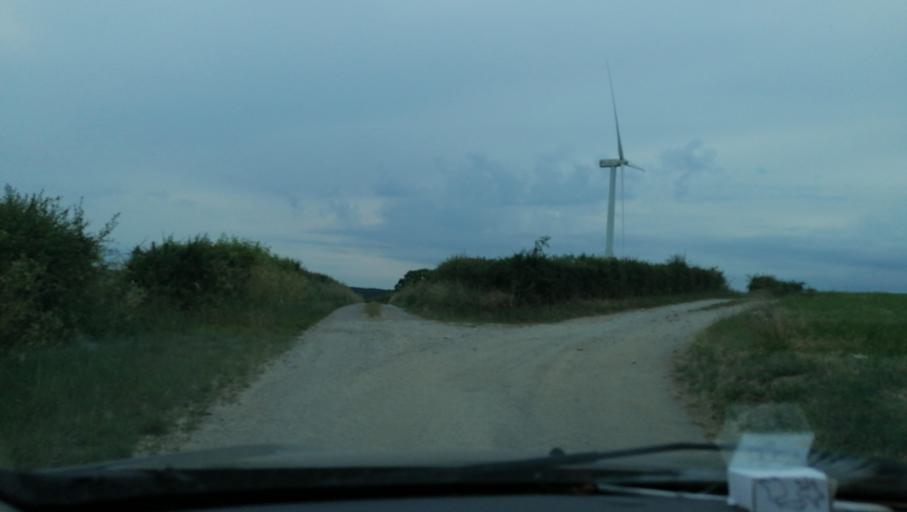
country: BE
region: Wallonia
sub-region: Province du Hainaut
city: Beaumont
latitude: 50.2053
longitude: 4.1625
